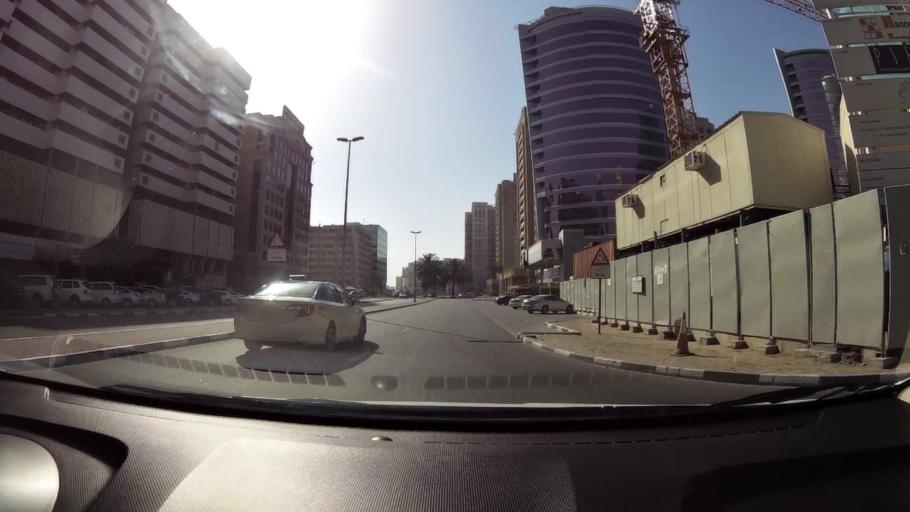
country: AE
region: Ash Shariqah
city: Sharjah
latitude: 25.2593
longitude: 55.3218
